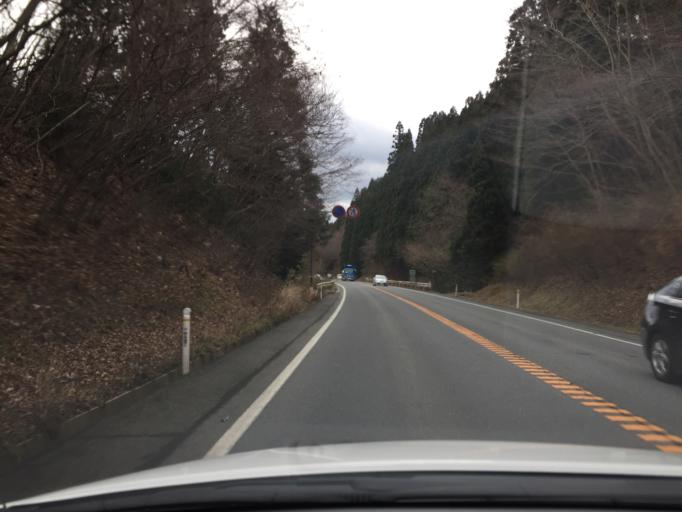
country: JP
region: Fukushima
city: Ishikawa
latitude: 37.1538
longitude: 140.6595
